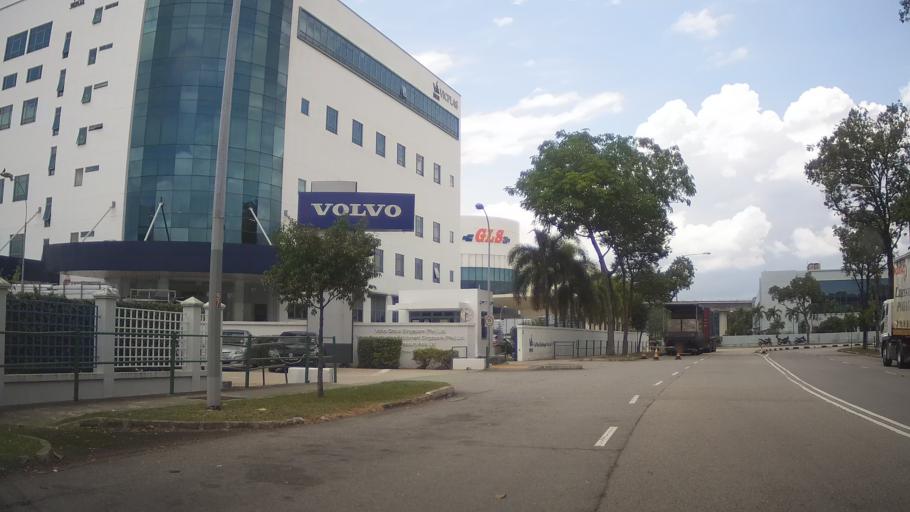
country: MY
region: Johor
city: Johor Bahru
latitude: 1.3239
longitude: 103.6673
